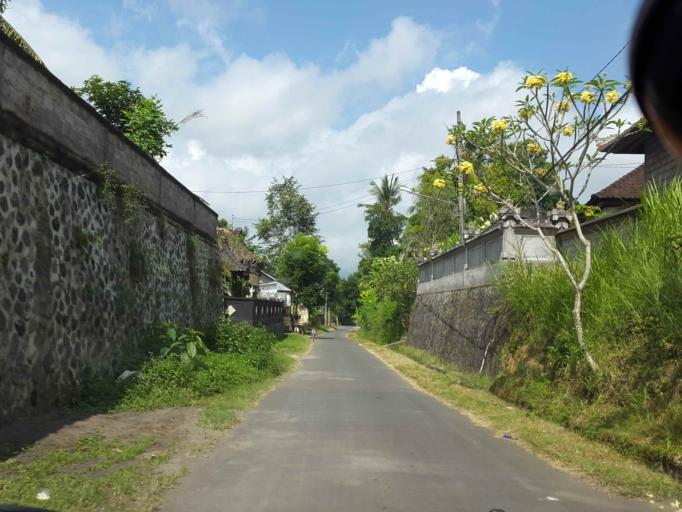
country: ID
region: Bali
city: Banjar Kelodan
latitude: -8.4984
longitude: 115.3637
